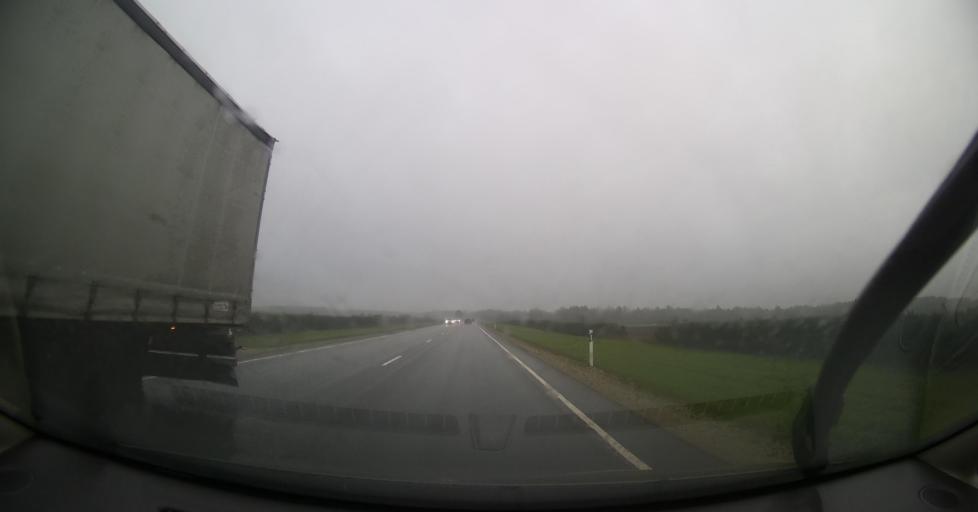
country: EE
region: Jogevamaa
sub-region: Poltsamaa linn
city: Poltsamaa
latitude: 58.6313
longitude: 26.1301
